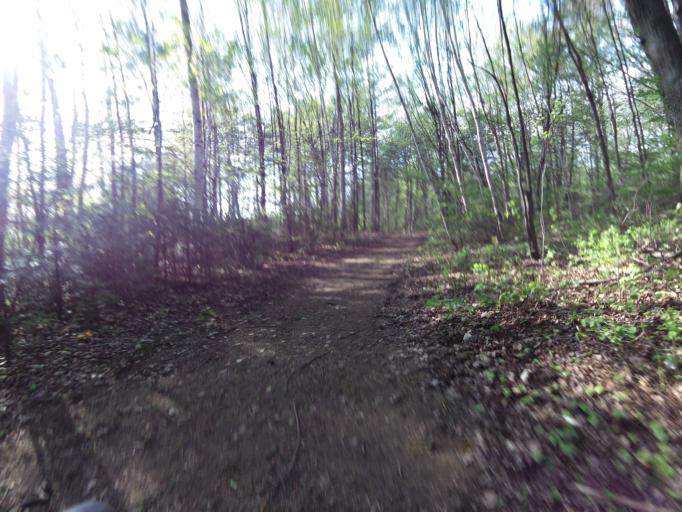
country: CA
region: Ontario
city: Ottawa
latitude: 45.3239
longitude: -75.7329
